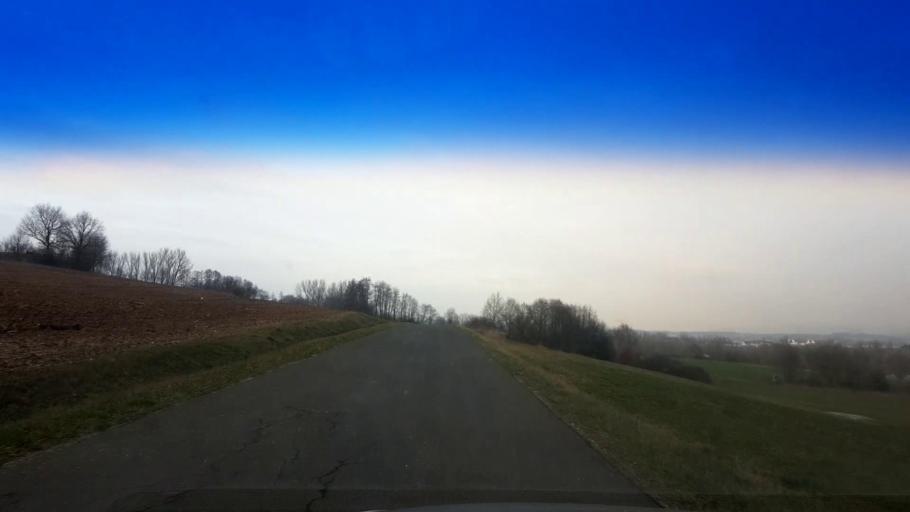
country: DE
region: Bavaria
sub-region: Upper Franconia
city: Hirschaid
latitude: 49.7974
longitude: 10.9938
